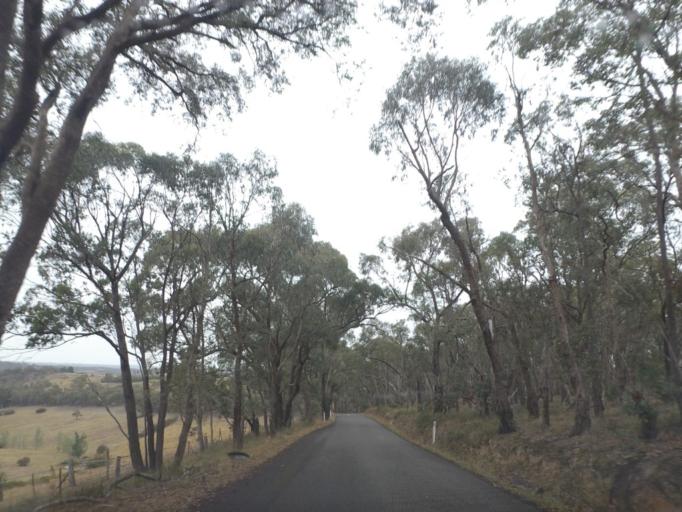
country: AU
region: Victoria
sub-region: Nillumbik
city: Saint Andrews
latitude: -37.6341
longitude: 145.2814
